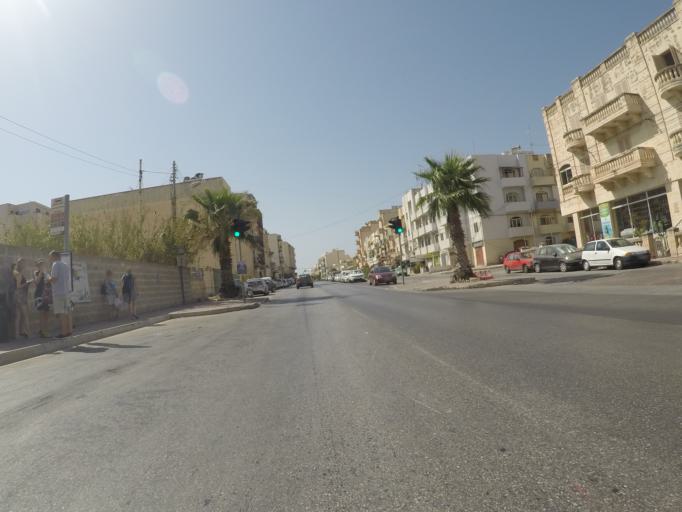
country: MT
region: Saint Paul's Bay
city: San Pawl il-Bahar
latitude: 35.9454
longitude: 14.4100
